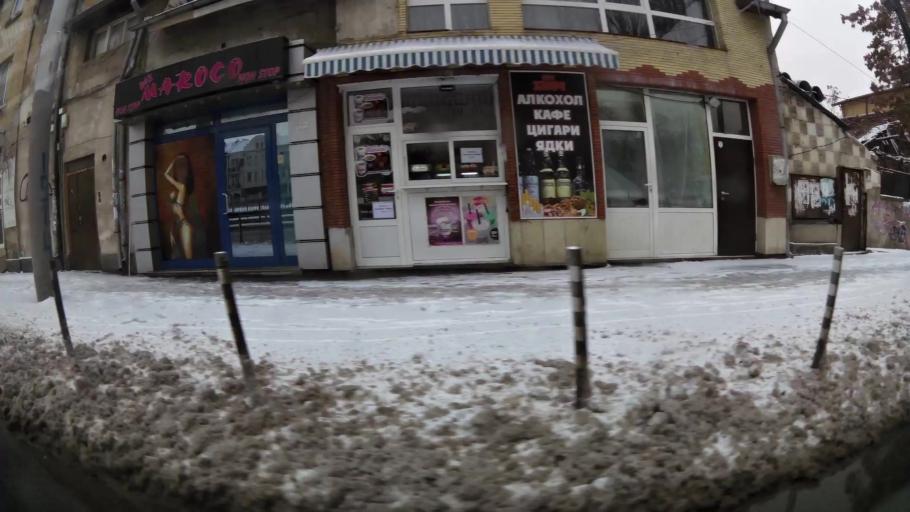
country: BG
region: Sofia-Capital
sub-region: Stolichna Obshtina
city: Sofia
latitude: 42.7048
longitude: 23.3219
